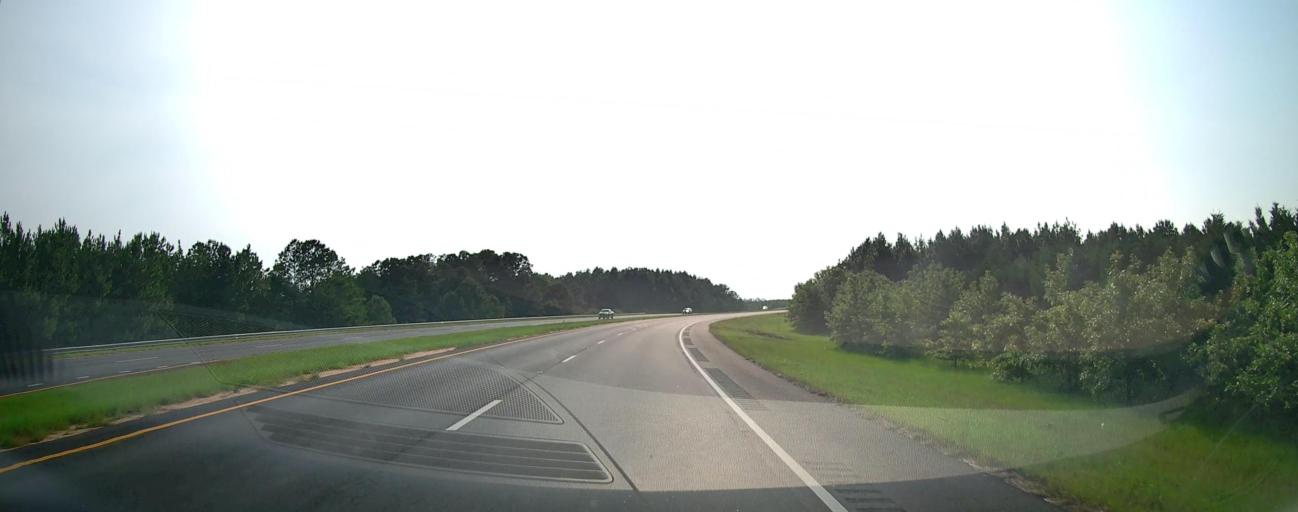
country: US
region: Georgia
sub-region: Taylor County
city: Butler
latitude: 32.5871
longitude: -84.3642
